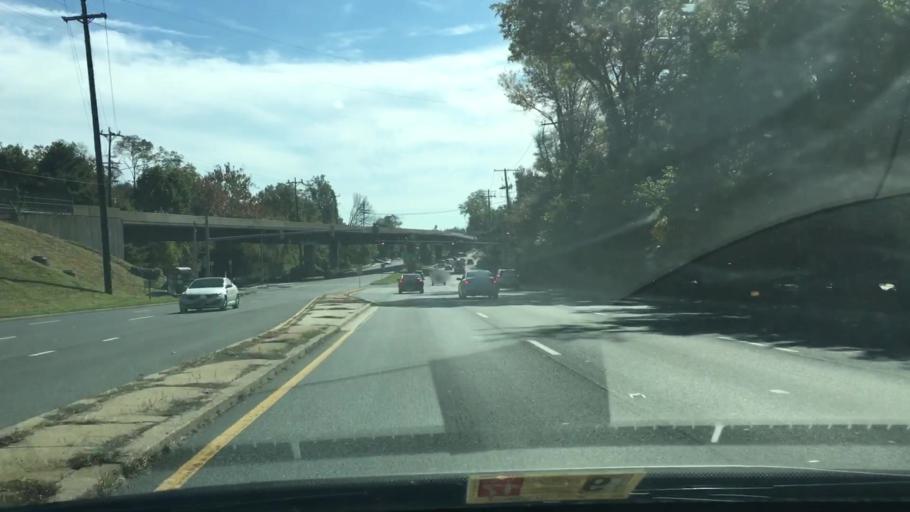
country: US
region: Maryland
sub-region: Montgomery County
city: South Kensington
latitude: 39.0252
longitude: -77.1033
